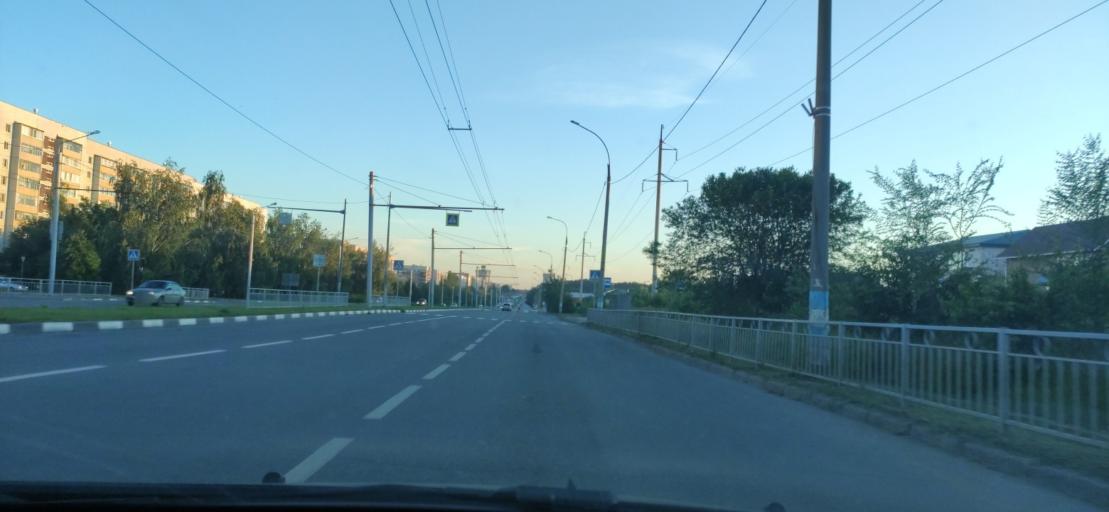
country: RU
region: Ulyanovsk
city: Mirnyy
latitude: 54.3876
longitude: 48.6092
